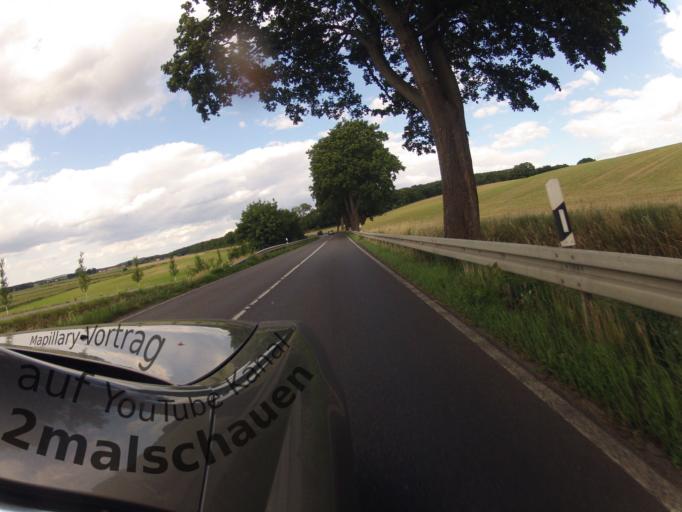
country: DE
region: Mecklenburg-Vorpommern
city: Seebad Heringsdorf
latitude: 53.8992
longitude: 14.1457
